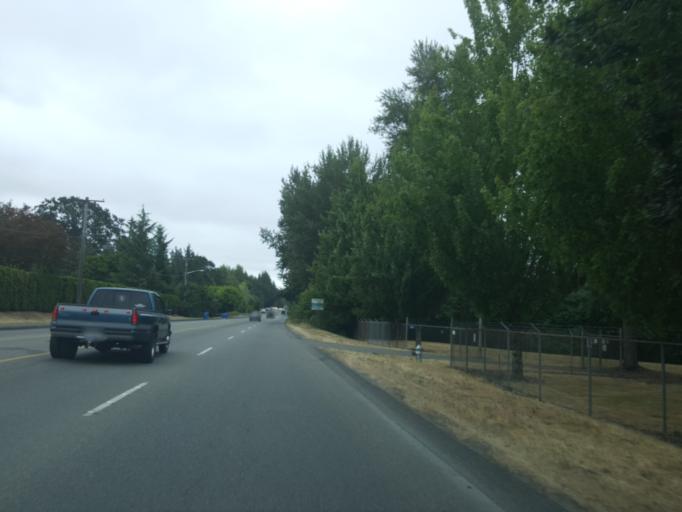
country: US
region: Washington
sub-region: Pierce County
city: Parkland
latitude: 47.1429
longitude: -122.4593
